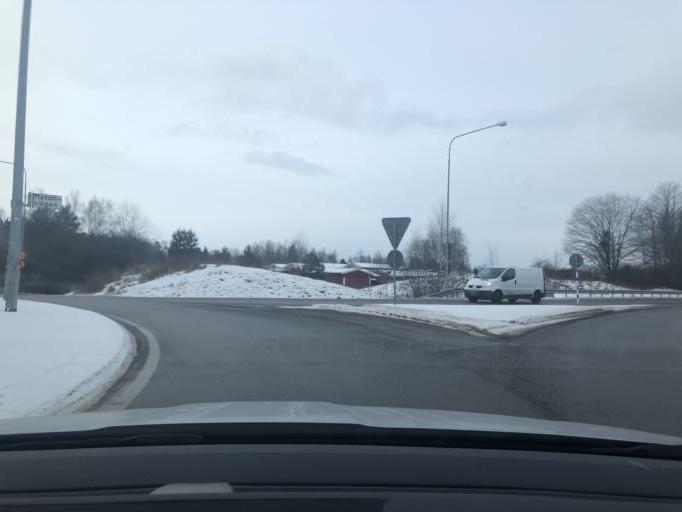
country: SE
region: OEstergoetland
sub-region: Motala Kommun
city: Motala
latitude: 58.5556
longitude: 15.0362
